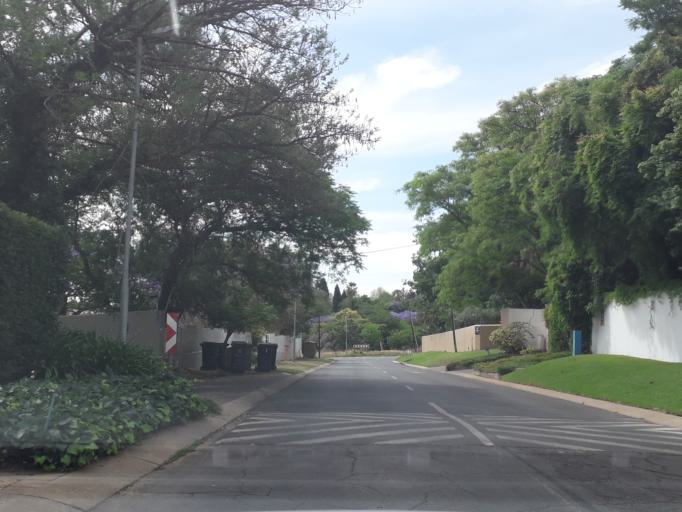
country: ZA
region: Gauteng
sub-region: City of Johannesburg Metropolitan Municipality
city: Diepsloot
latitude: -26.0611
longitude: 28.0170
